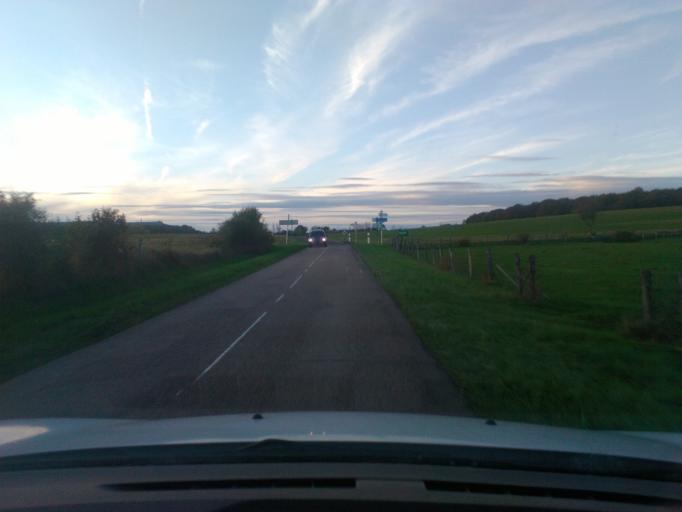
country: FR
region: Lorraine
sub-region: Departement de Meurthe-et-Moselle
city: Vezelise
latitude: 48.4070
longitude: 6.1496
